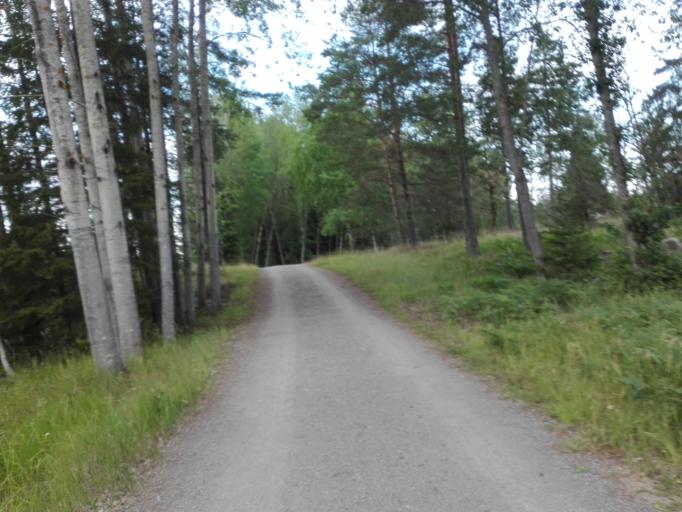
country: SE
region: Stockholm
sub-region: Nacka Kommun
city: Fisksatra
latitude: 59.2851
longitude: 18.2354
